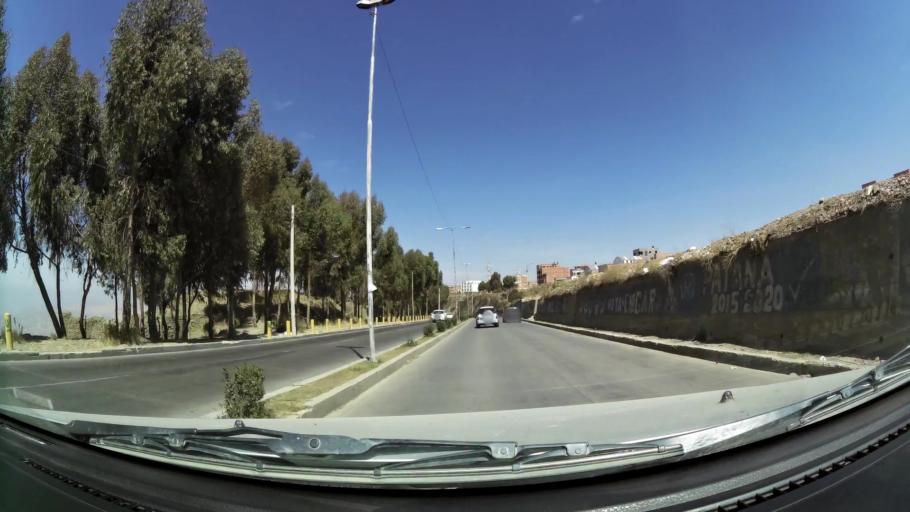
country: BO
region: La Paz
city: La Paz
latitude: -16.5313
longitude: -68.1478
